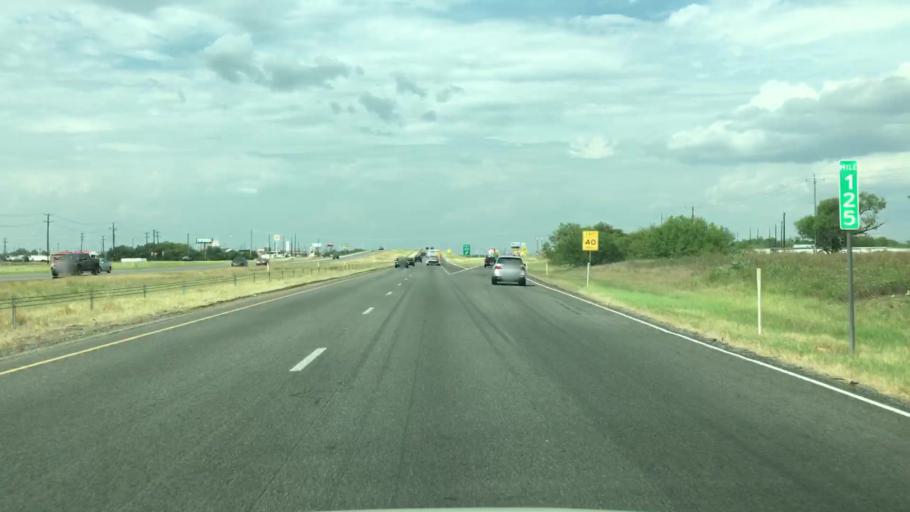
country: US
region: Texas
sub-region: Bexar County
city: Elmendorf
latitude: 29.2118
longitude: -98.4149
